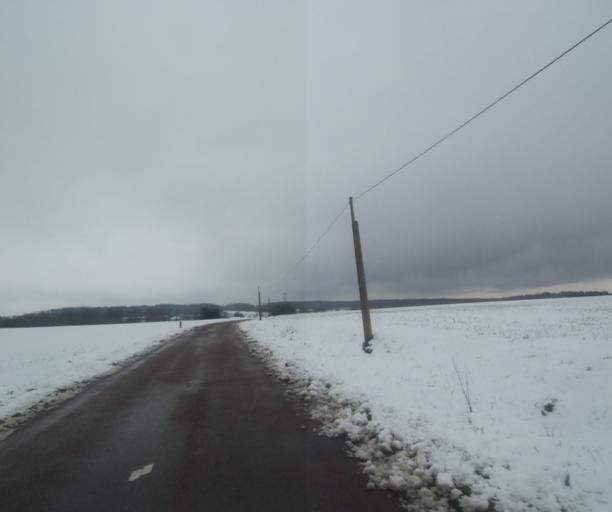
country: FR
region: Champagne-Ardenne
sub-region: Departement de la Haute-Marne
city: Laneuville-a-Remy
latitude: 48.5063
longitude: 4.8516
